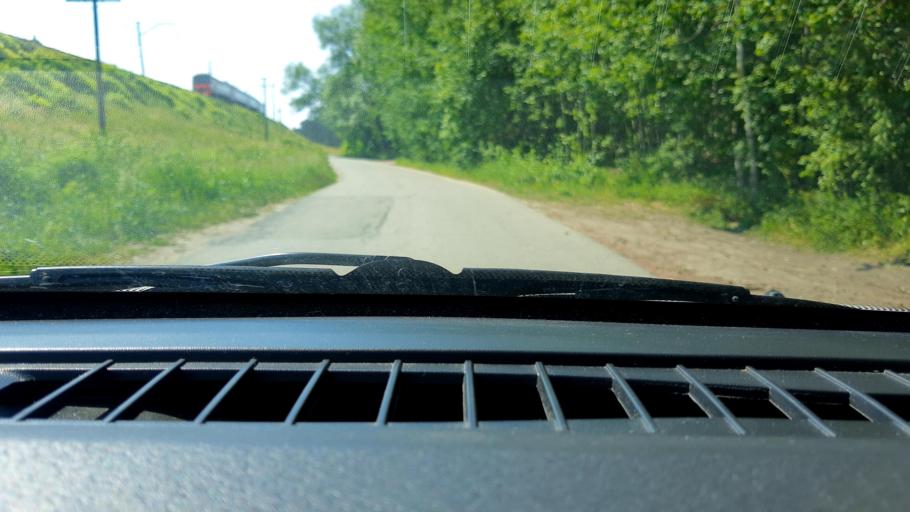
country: RU
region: Nizjnij Novgorod
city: Burevestnik
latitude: 56.1988
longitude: 43.8031
